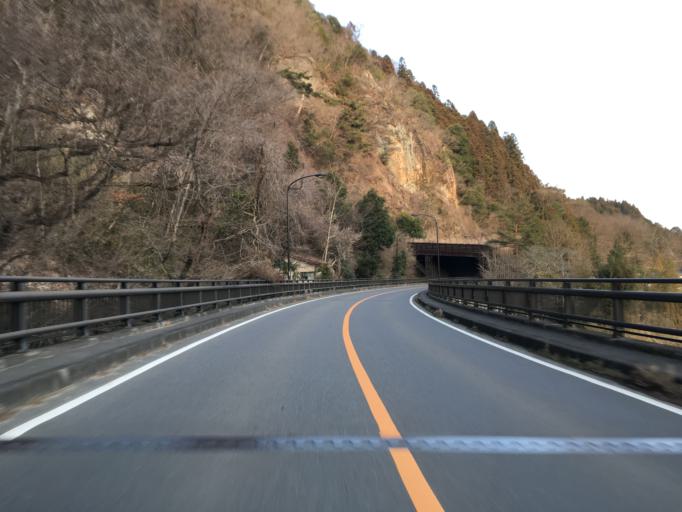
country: JP
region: Ibaraki
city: Daigo
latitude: 36.8543
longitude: 140.4009
